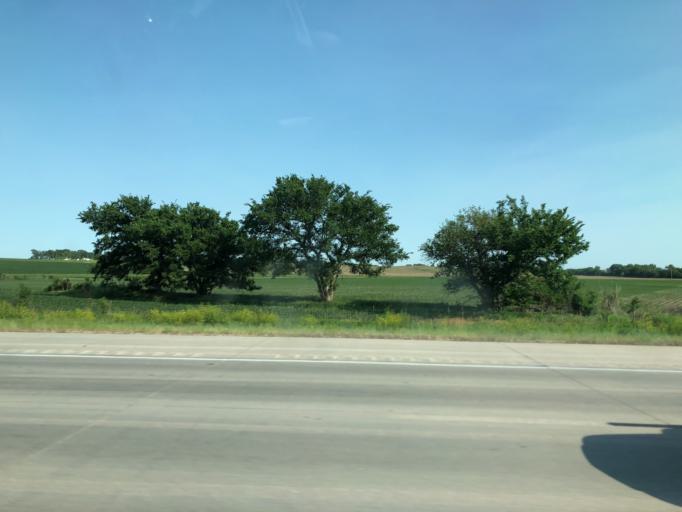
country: US
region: Nebraska
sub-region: Lancaster County
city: Waverly
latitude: 40.9147
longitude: -96.4782
